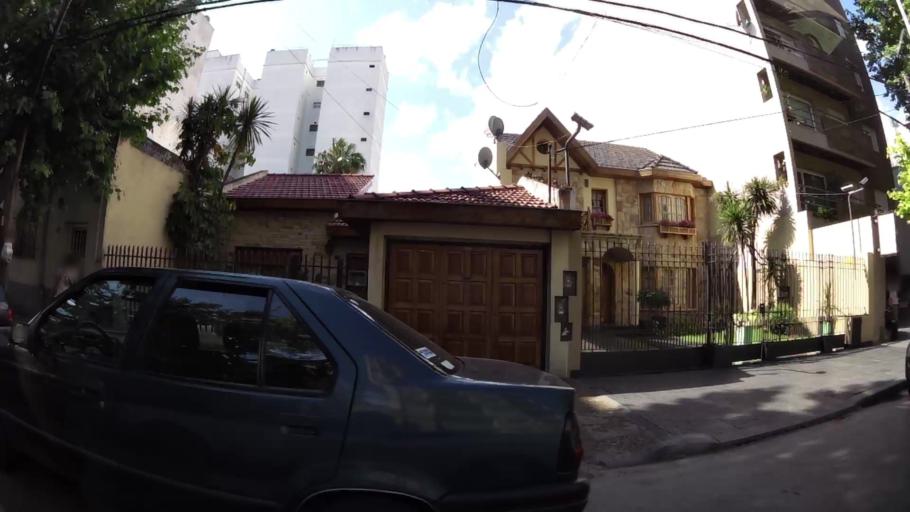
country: AR
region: Buenos Aires
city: San Justo
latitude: -34.6442
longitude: -58.5627
